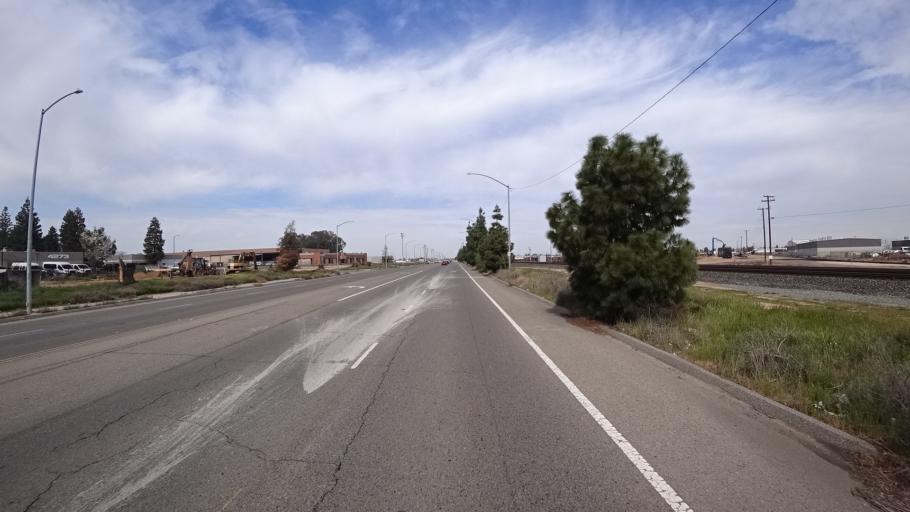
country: US
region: California
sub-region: Fresno County
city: West Park
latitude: 36.7969
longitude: -119.8650
